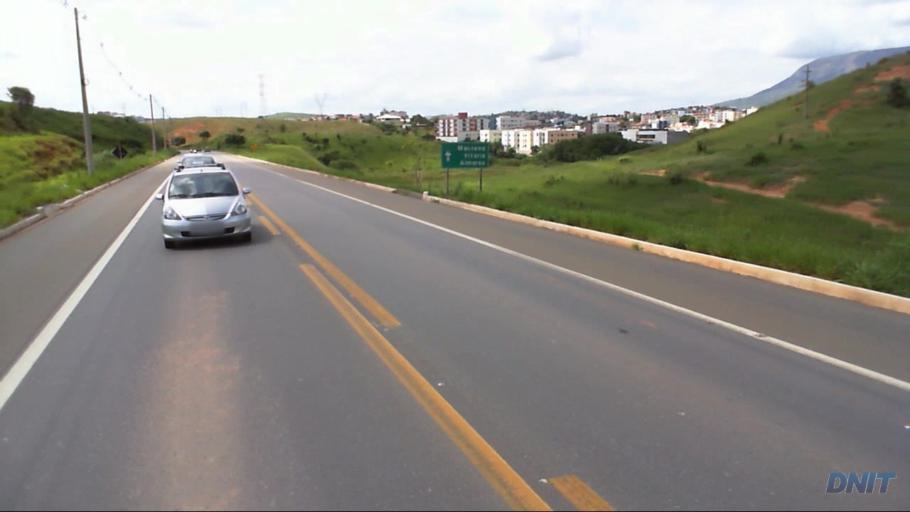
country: BR
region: Minas Gerais
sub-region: Governador Valadares
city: Governador Valadares
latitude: -18.8424
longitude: -41.9702
